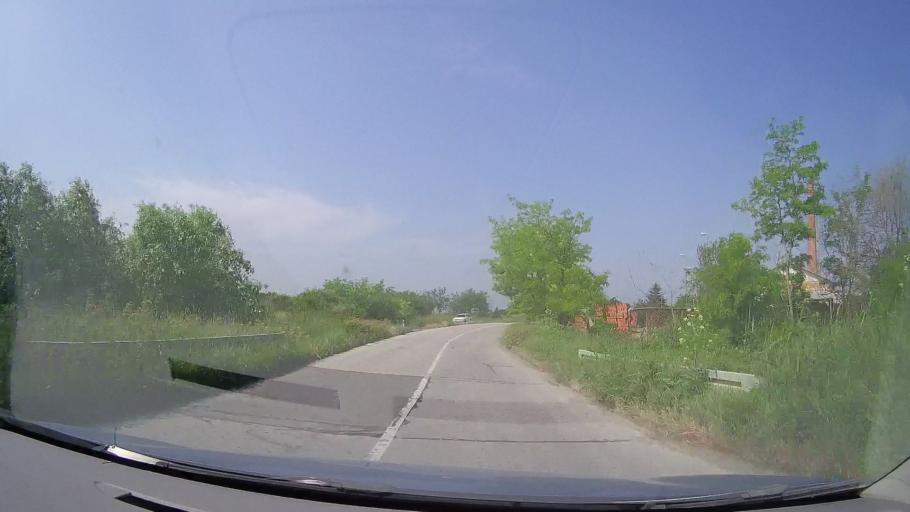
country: RS
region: Autonomna Pokrajina Vojvodina
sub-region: Srednjebanatski Okrug
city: Secanj
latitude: 45.3534
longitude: 20.7650
